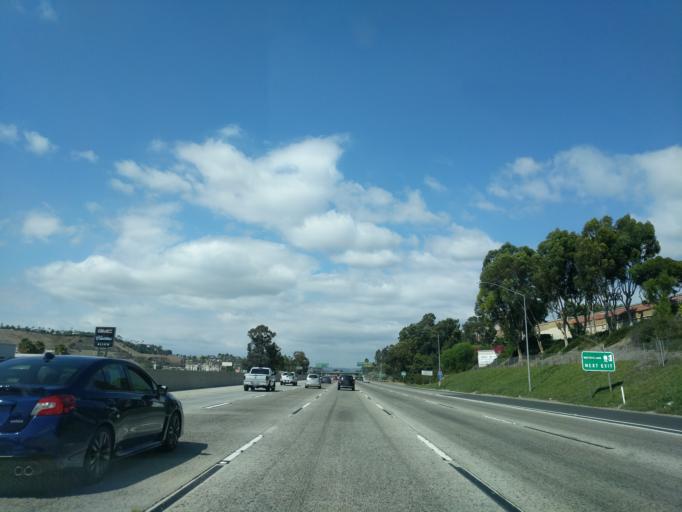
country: US
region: California
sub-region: Orange County
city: Ladera Ranch
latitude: 33.5504
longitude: -117.6727
